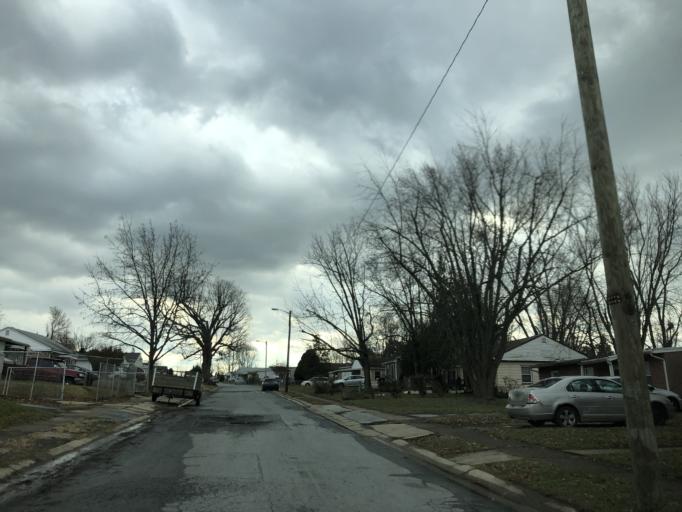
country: US
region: Delaware
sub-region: New Castle County
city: Wilmington Manor
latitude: 39.7095
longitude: -75.5565
